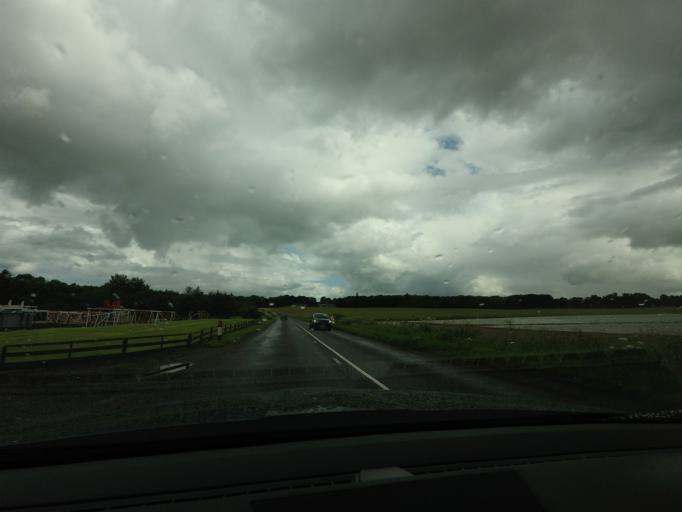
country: GB
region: Scotland
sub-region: Aberdeenshire
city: Turriff
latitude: 57.5531
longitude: -2.4406
